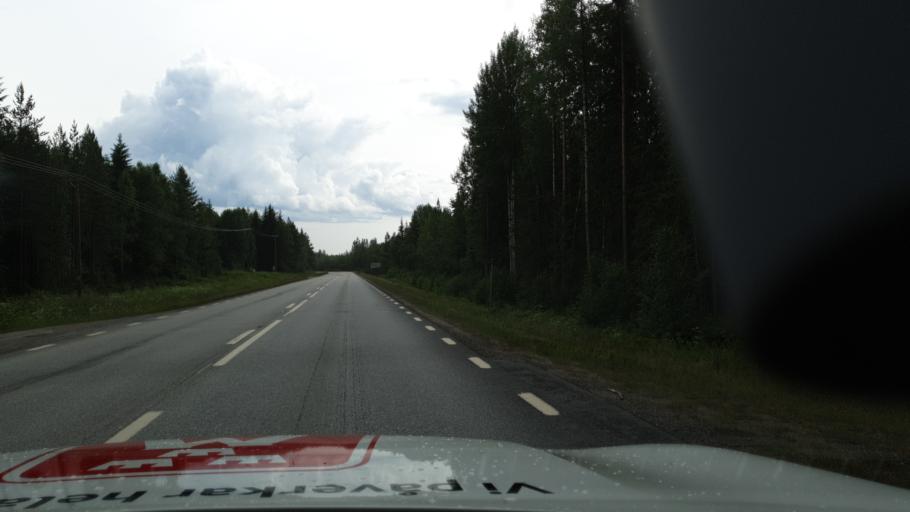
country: SE
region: Vaesterbotten
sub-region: Vannas Kommun
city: Vaennaes
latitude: 63.9371
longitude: 19.7714
